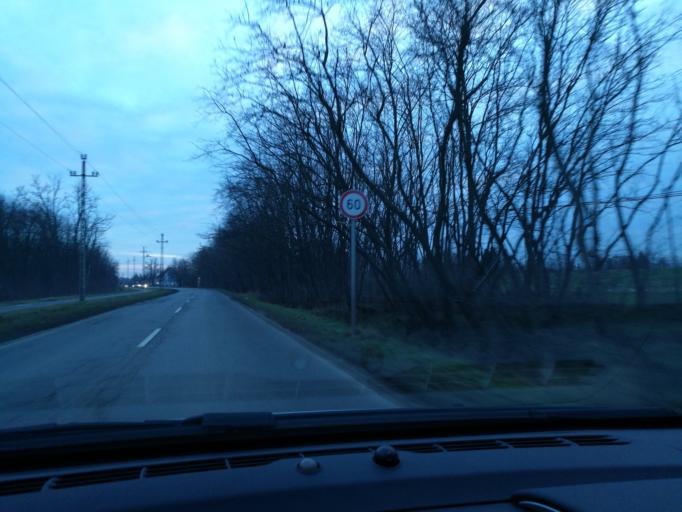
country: HU
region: Szabolcs-Szatmar-Bereg
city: Nyiregyhaza
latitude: 47.9794
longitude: 21.7050
